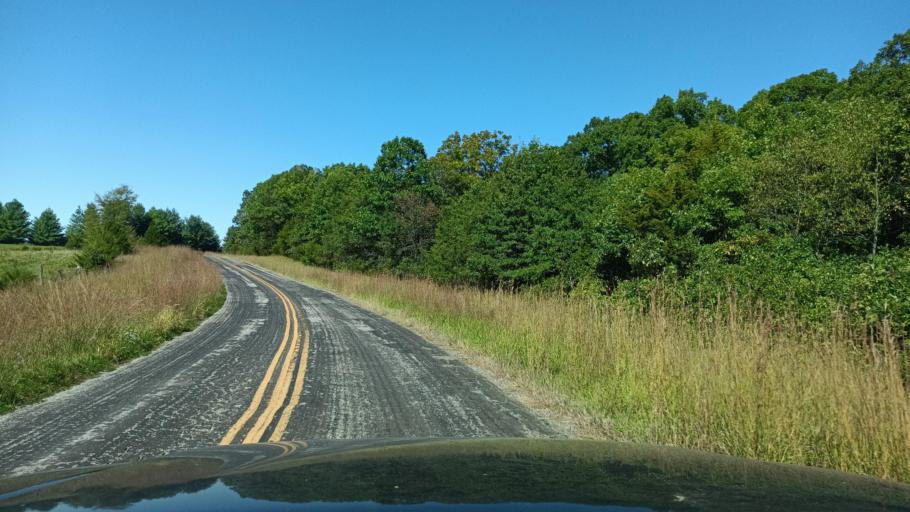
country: US
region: Missouri
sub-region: Scotland County
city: Memphis
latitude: 40.3563
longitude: -92.3555
